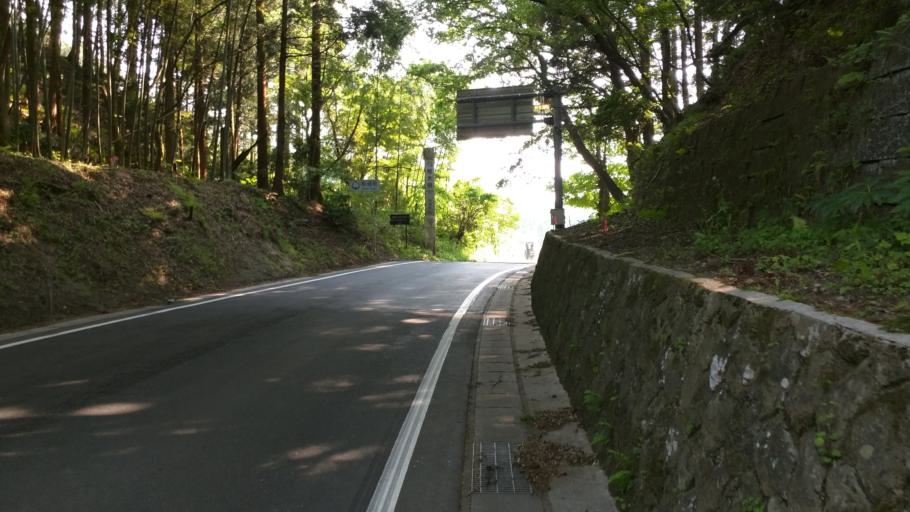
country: JP
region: Tochigi
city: Kuroiso
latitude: 37.0691
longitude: 140.1859
